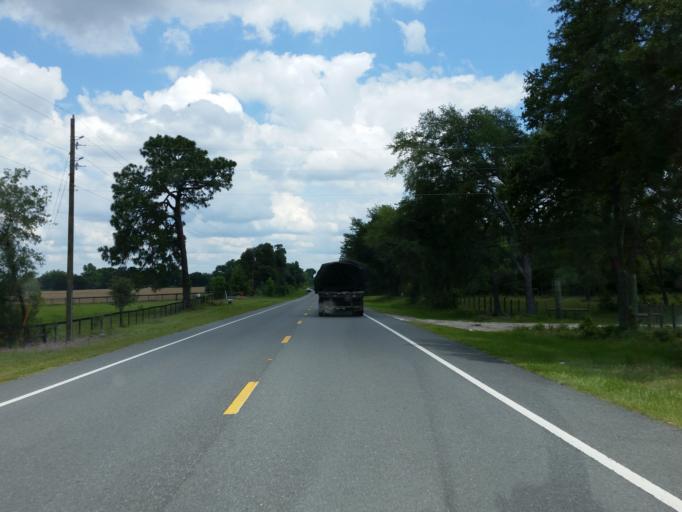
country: US
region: Florida
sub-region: Levy County
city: Williston Highlands
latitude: 29.2354
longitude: -82.4412
